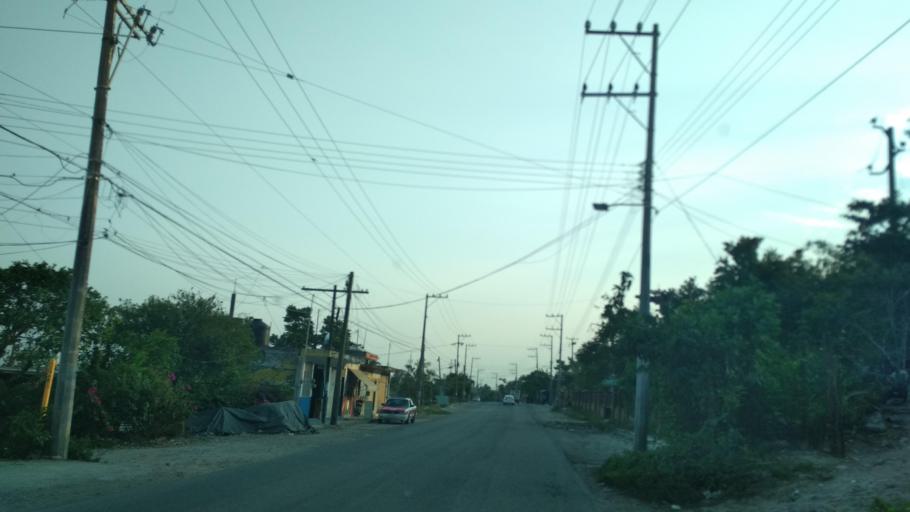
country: MM
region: Shan
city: Taunggyi
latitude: 20.4115
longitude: 97.3368
